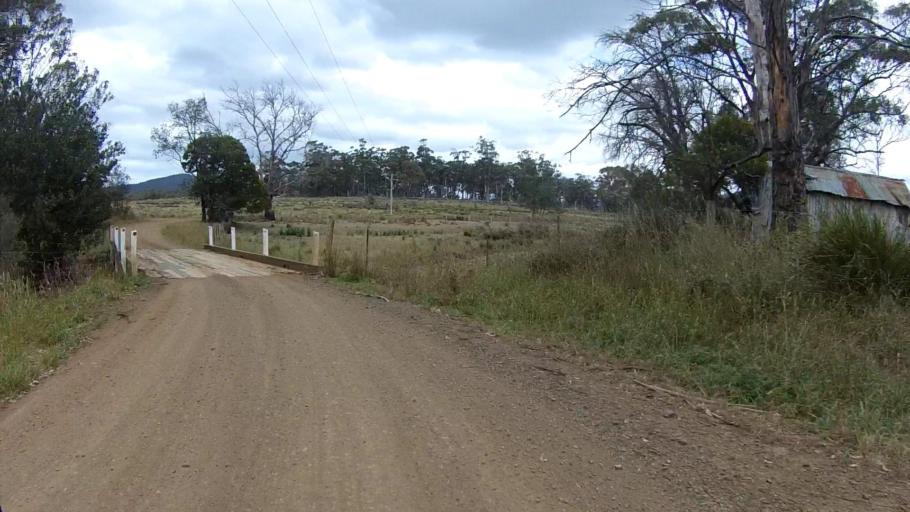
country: AU
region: Tasmania
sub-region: Sorell
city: Sorell
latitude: -42.6409
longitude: 147.9070
